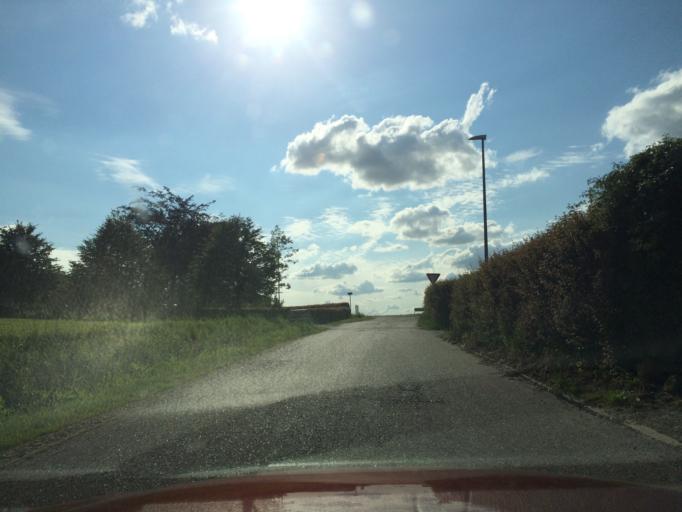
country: DK
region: Central Jutland
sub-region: Viborg Kommune
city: Bjerringbro
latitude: 56.2514
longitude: 9.7049
